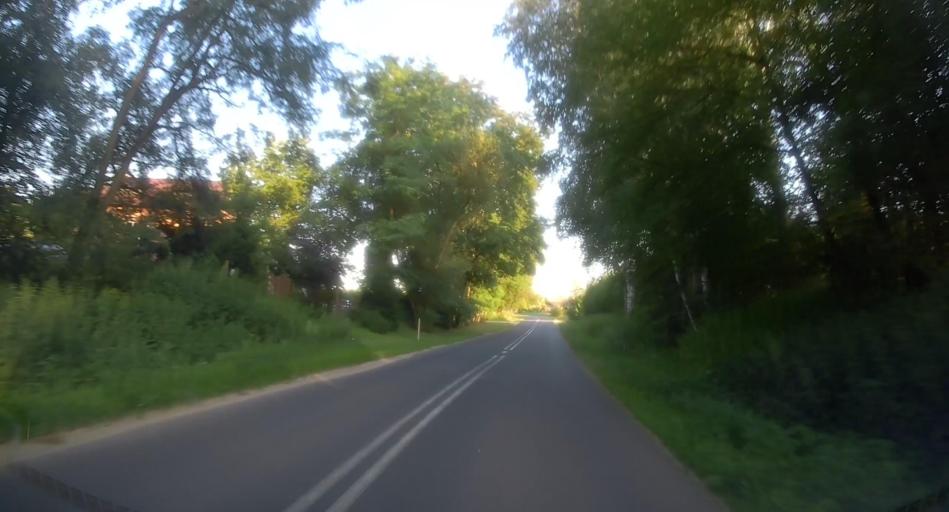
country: PL
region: Lodz Voivodeship
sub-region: Powiat skierniewicki
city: Kowiesy
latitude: 51.8962
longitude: 20.3795
